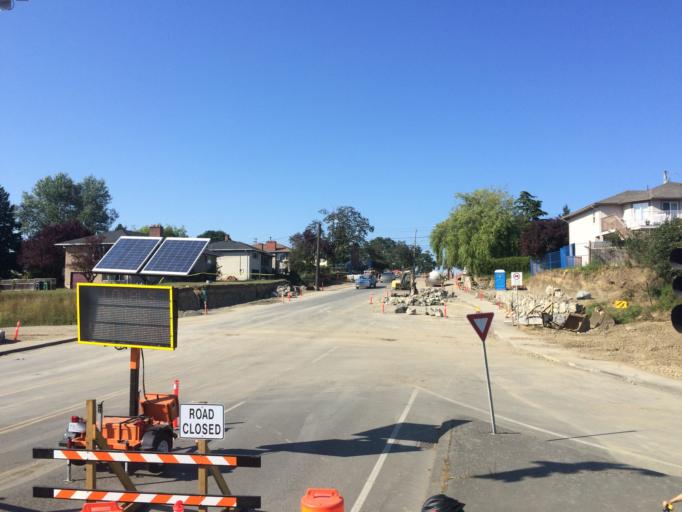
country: CA
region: British Columbia
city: Victoria
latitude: 48.4582
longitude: -123.3901
